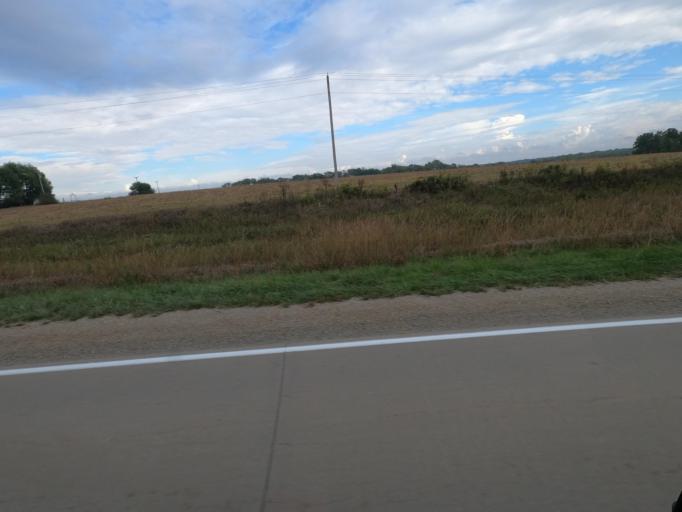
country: US
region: Iowa
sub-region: Henry County
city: Mount Pleasant
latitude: 40.7980
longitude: -91.7045
